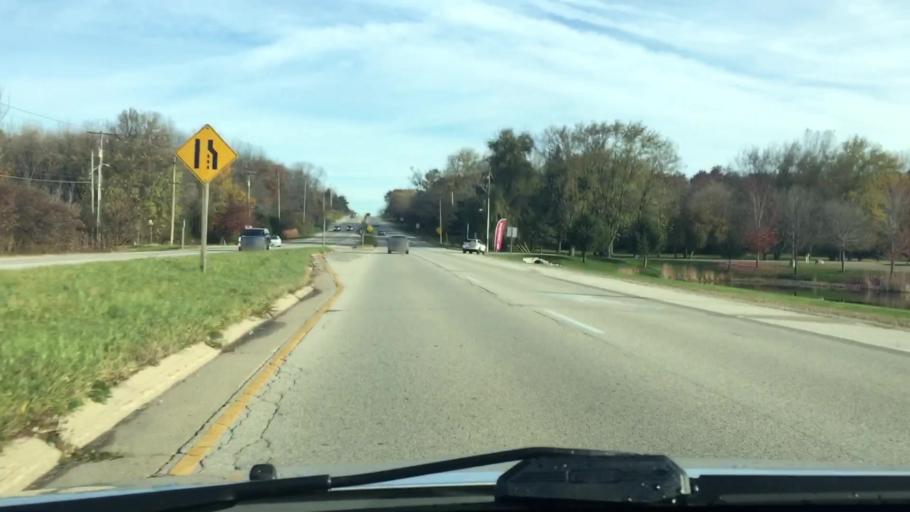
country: US
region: Wisconsin
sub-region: Waukesha County
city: Delafield
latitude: 43.0633
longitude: -88.3678
